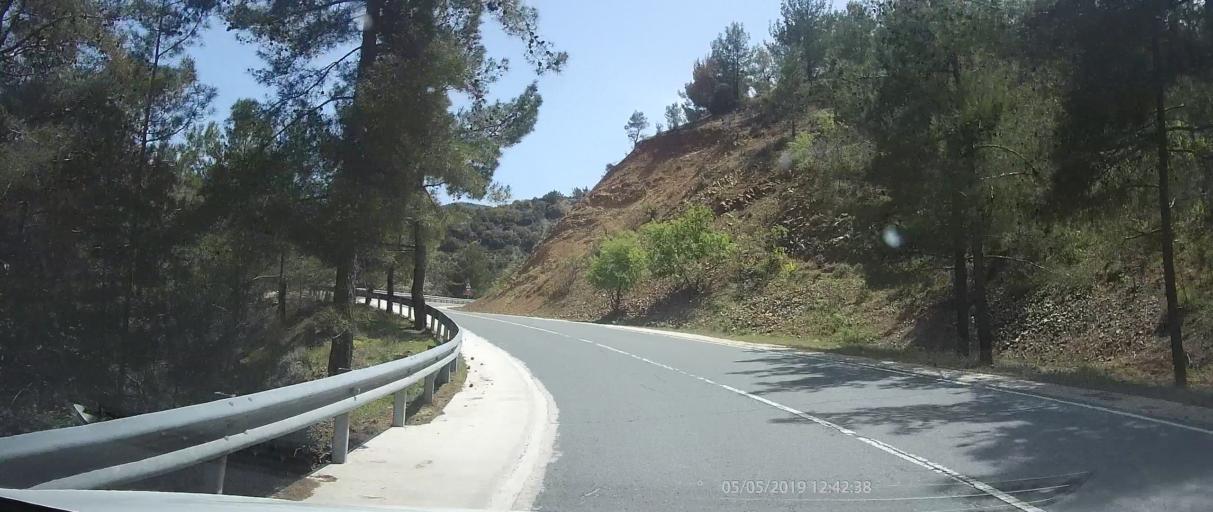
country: CY
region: Lefkosia
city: Kakopetria
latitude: 34.9726
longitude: 32.8114
